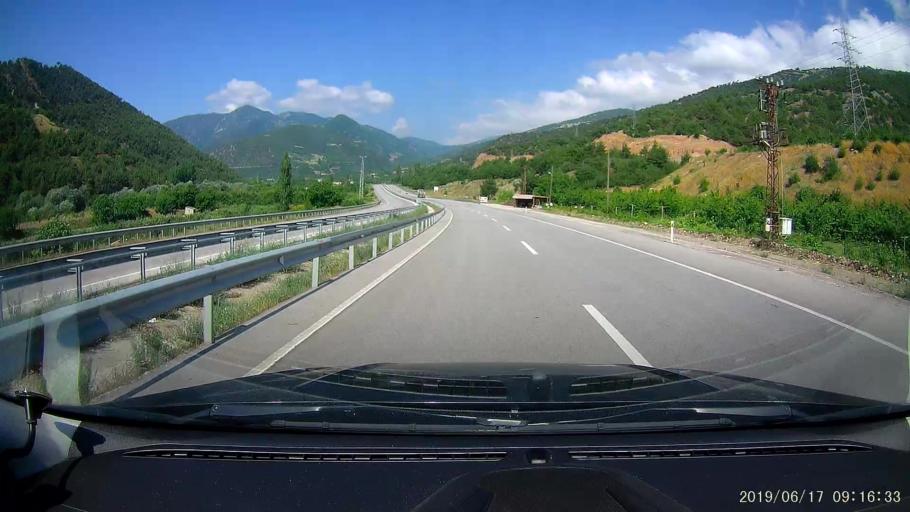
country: TR
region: Amasya
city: Akdag
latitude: 40.7441
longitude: 36.0085
